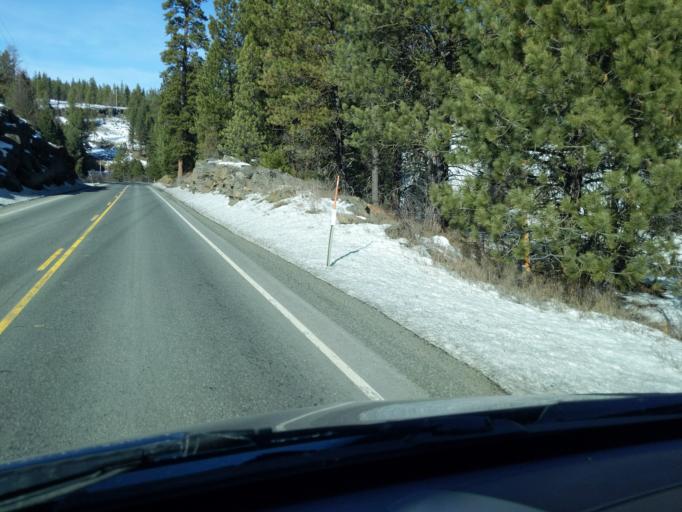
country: US
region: Oregon
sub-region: Grant County
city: John Day
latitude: 44.9322
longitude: -119.0105
